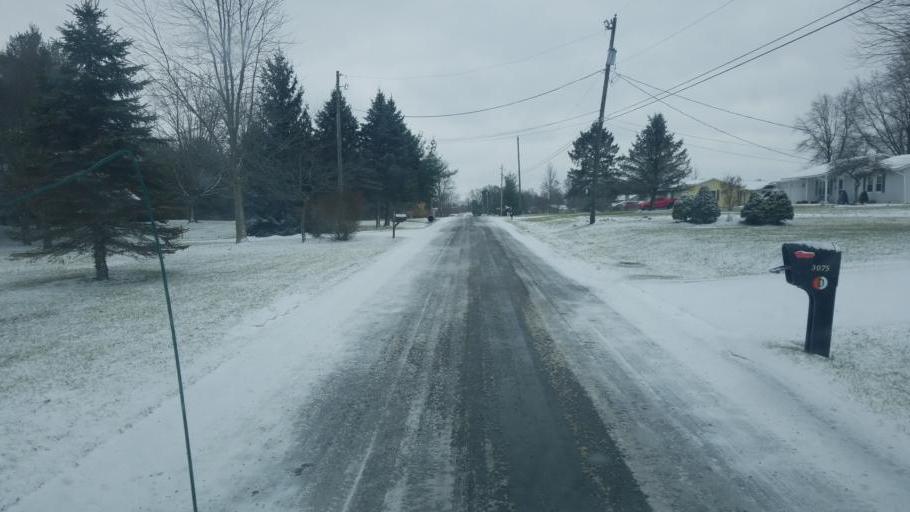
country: US
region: Ohio
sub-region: Delaware County
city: Sunbury
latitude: 40.2444
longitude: -82.7729
